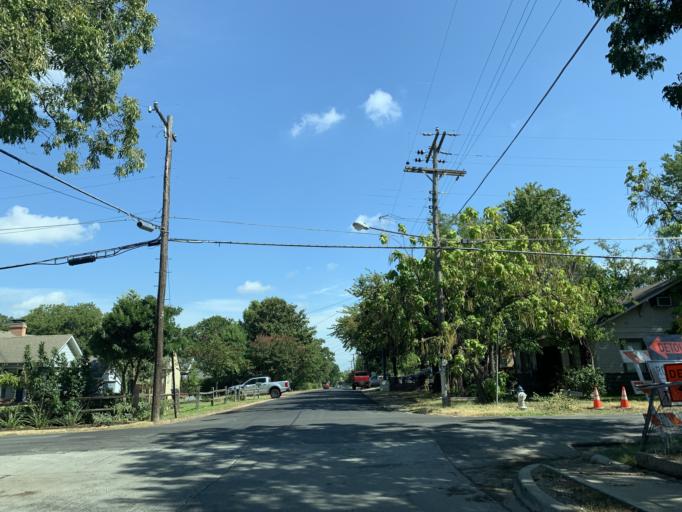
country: US
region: Texas
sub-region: Dallas County
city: Cockrell Hill
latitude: 32.7384
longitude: -96.8728
